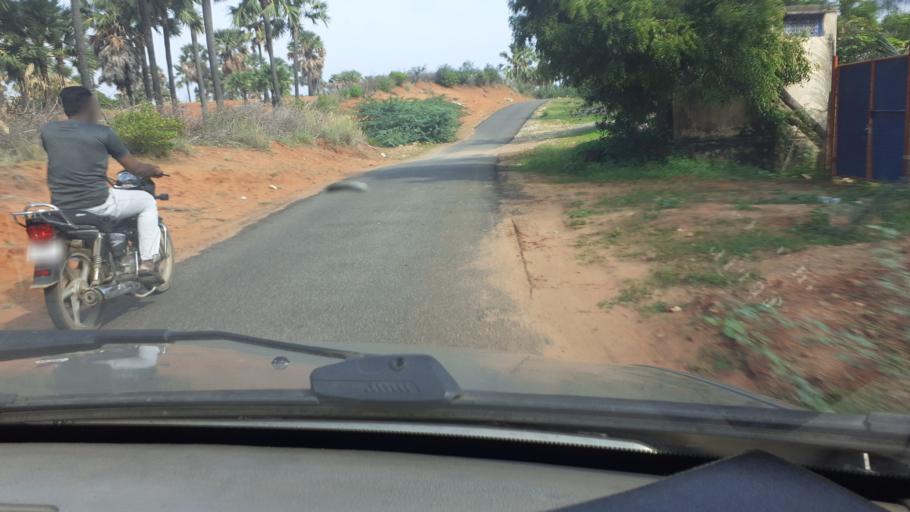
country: IN
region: Tamil Nadu
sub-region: Tirunelveli Kattabo
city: Tisaiyanvilai
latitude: 8.3375
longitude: 77.9467
